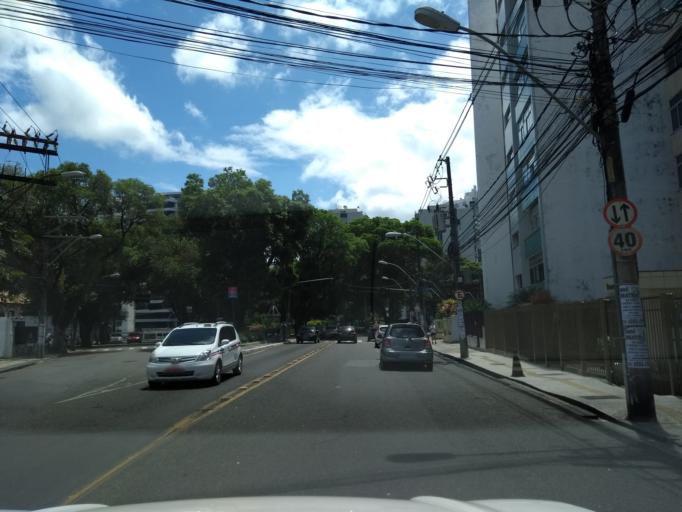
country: BR
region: Bahia
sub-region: Salvador
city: Salvador
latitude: -12.9989
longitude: -38.5229
